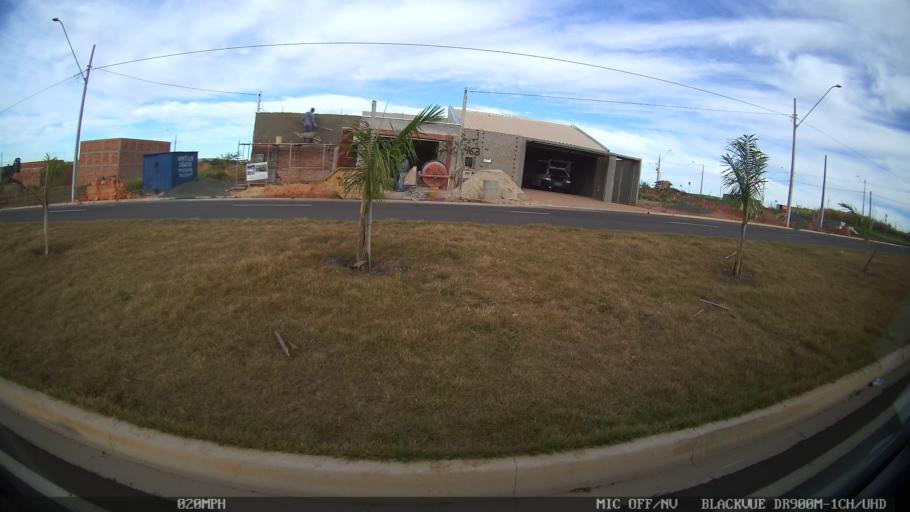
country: BR
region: Sao Paulo
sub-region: Catanduva
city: Catanduva
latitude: -21.1382
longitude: -49.0109
